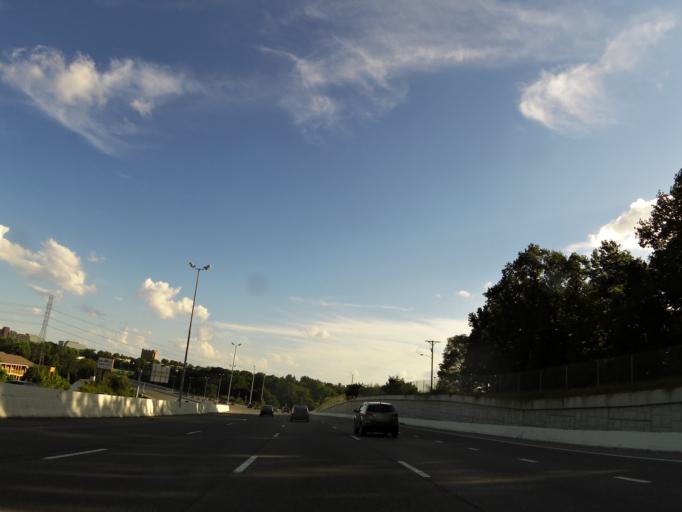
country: US
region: Tennessee
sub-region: Davidson County
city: Nashville
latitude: 36.1605
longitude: -86.6919
